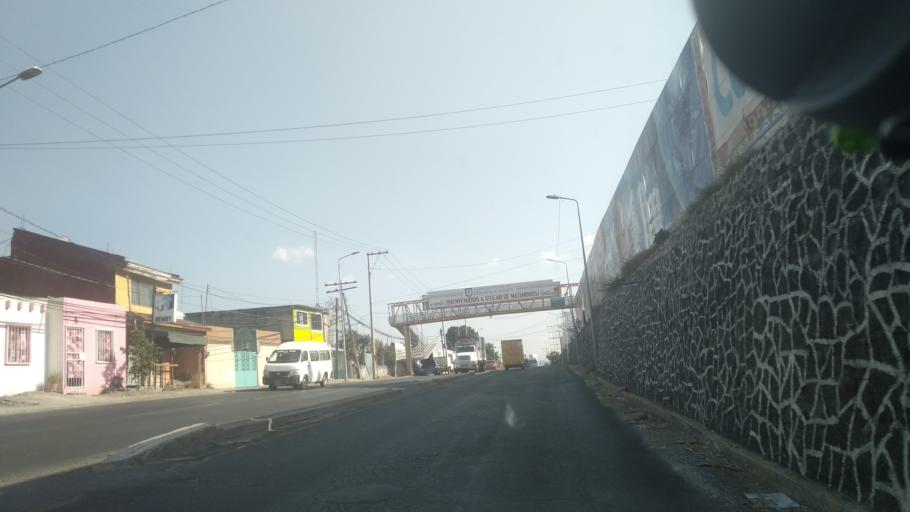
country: MX
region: Puebla
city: Izucar de Matamoros
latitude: 18.6117
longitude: -98.4656
